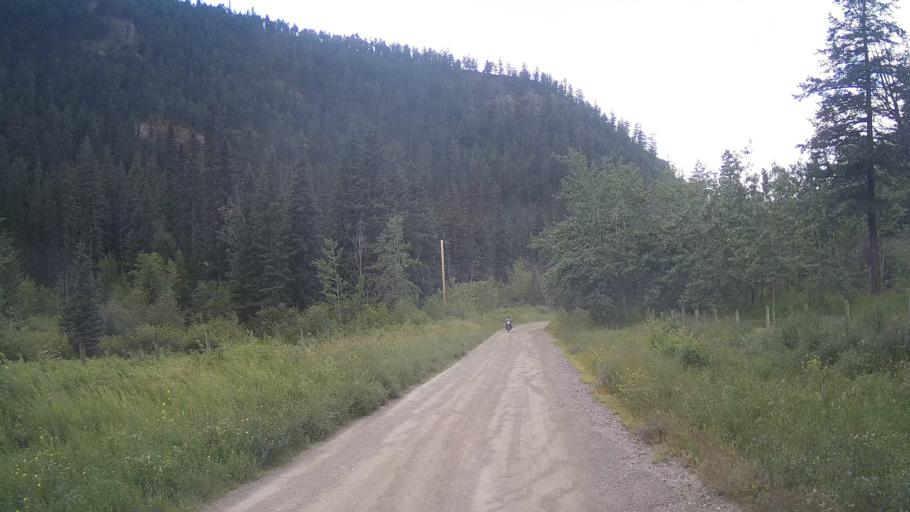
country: CA
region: British Columbia
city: Lillooet
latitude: 51.2519
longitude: -122.0136
